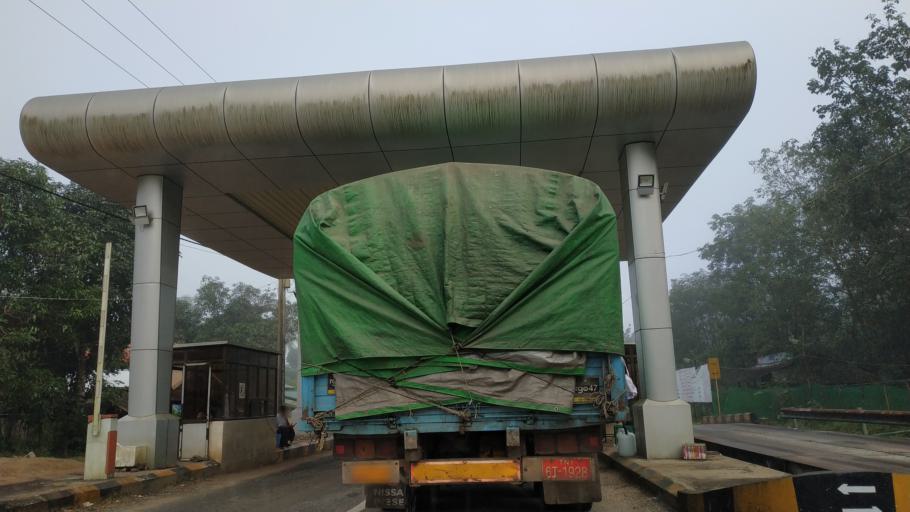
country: MM
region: Tanintharyi
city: Dawei
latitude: 14.1865
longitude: 98.2064
